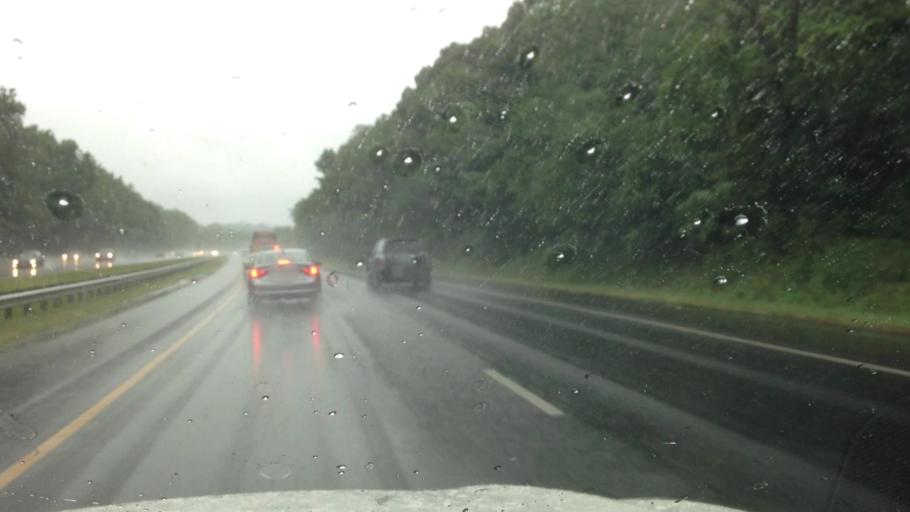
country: US
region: Maryland
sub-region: Prince George's County
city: Landover
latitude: 38.9239
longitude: -76.9035
